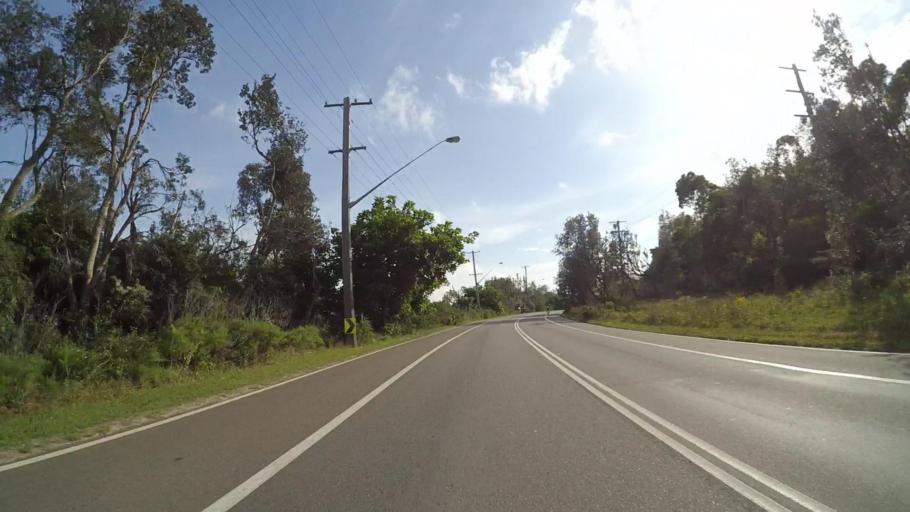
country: AU
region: New South Wales
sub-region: Rockdale
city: Dolls Point
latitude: -34.0248
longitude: 151.1643
